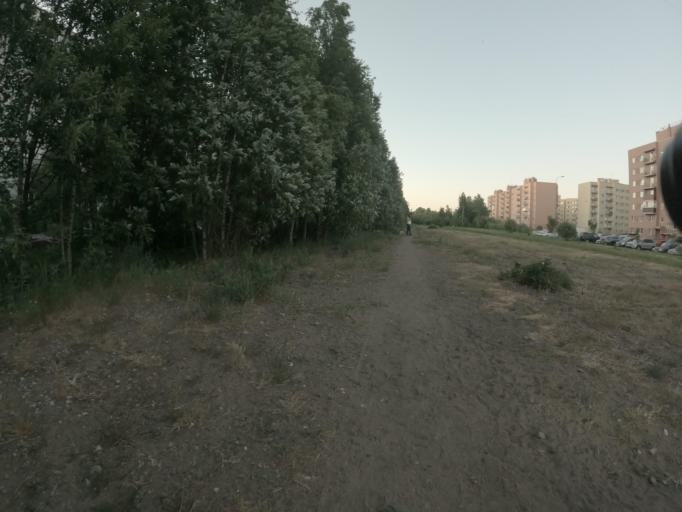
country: RU
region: St.-Petersburg
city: Krasnogvargeisky
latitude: 59.9840
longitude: 30.5237
